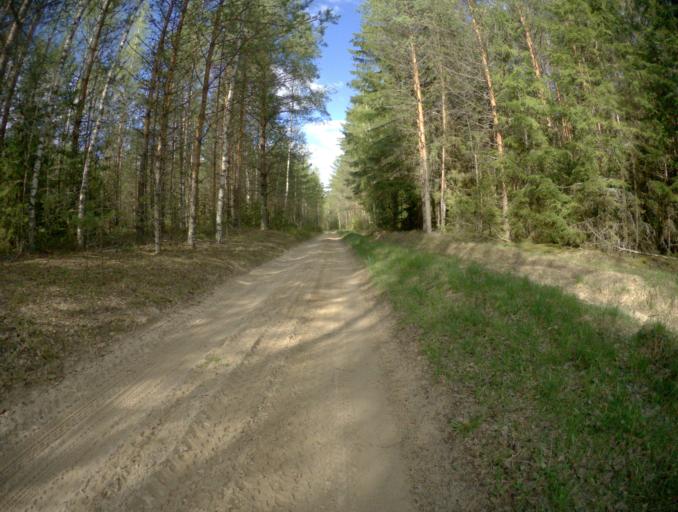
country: RU
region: Vladimir
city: Golovino
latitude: 55.8933
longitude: 40.4153
